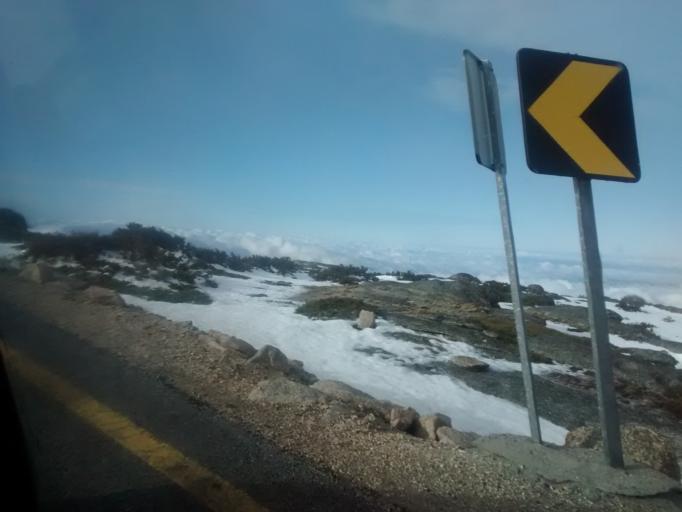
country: PT
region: Guarda
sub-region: Seia
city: Seia
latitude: 40.3477
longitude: -7.6631
